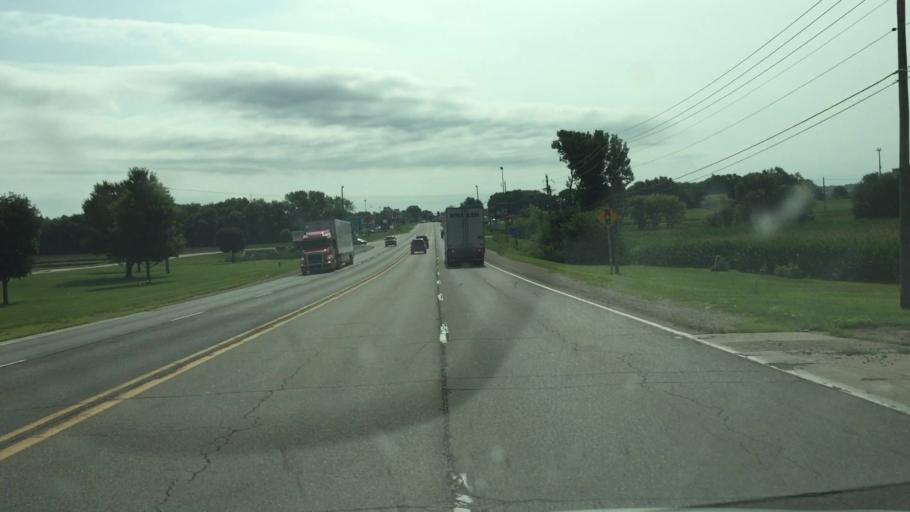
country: US
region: Iowa
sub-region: Lee County
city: Fort Madison
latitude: 40.6242
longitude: -91.3847
